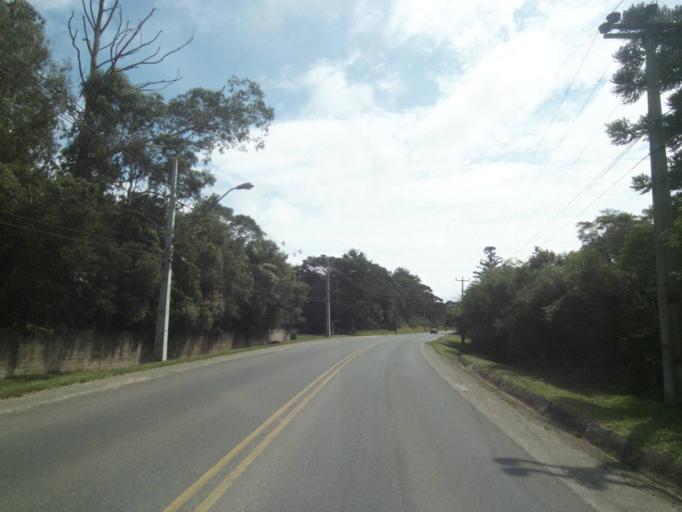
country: BR
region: Parana
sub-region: Campina Grande Do Sul
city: Campina Grande do Sul
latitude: -25.3109
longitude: -49.0673
